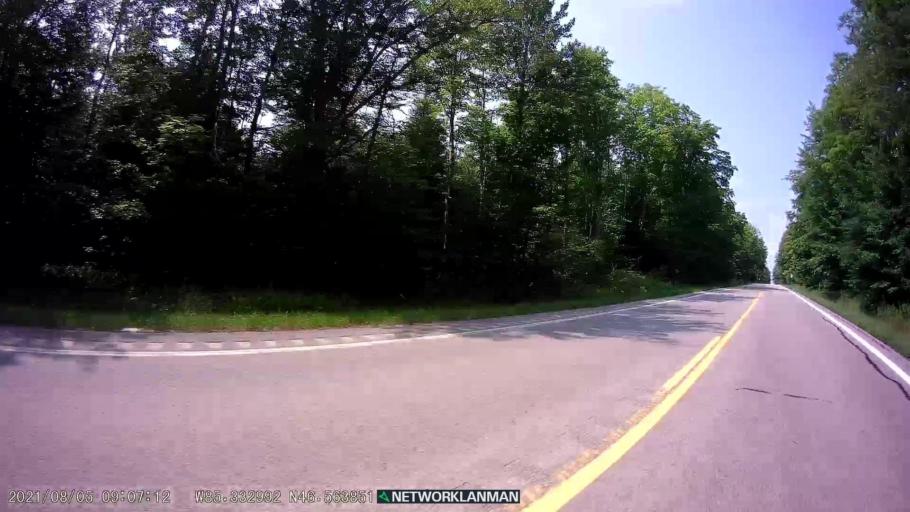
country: US
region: Michigan
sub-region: Luce County
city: Newberry
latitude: 46.5639
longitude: -85.3333
